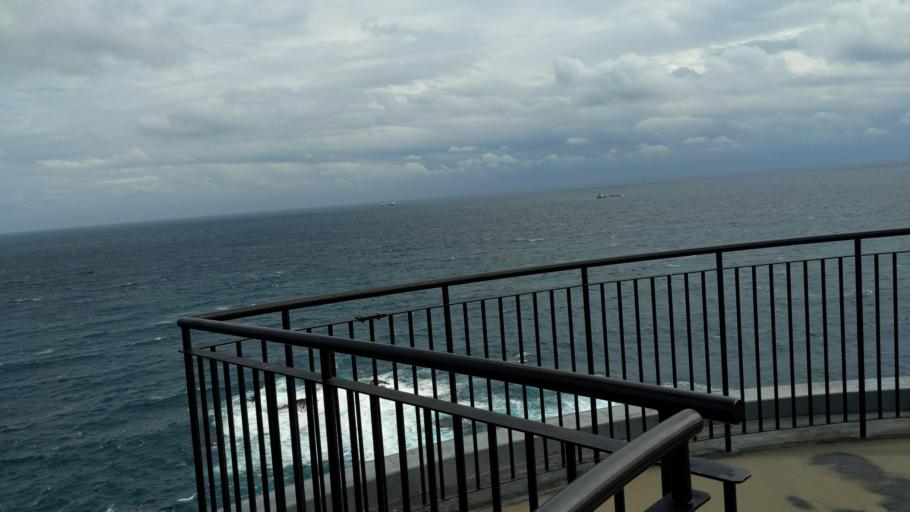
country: JP
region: Wakayama
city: Shingu
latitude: 33.4716
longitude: 135.8619
